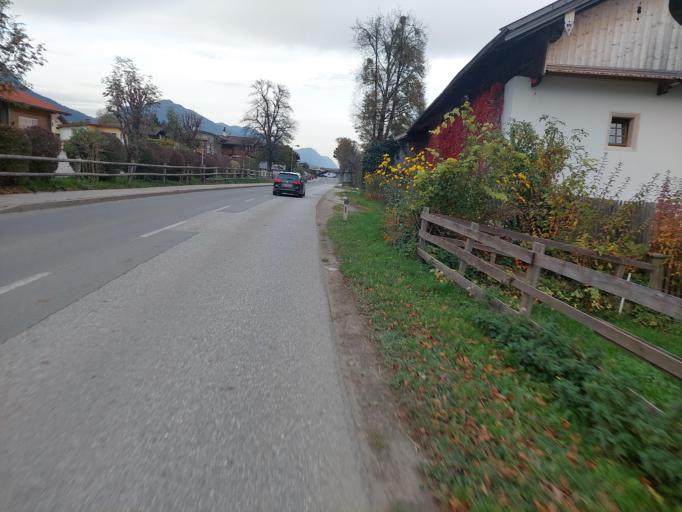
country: AT
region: Tyrol
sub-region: Politischer Bezirk Kufstein
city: Munster
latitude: 47.4101
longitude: 11.8274
